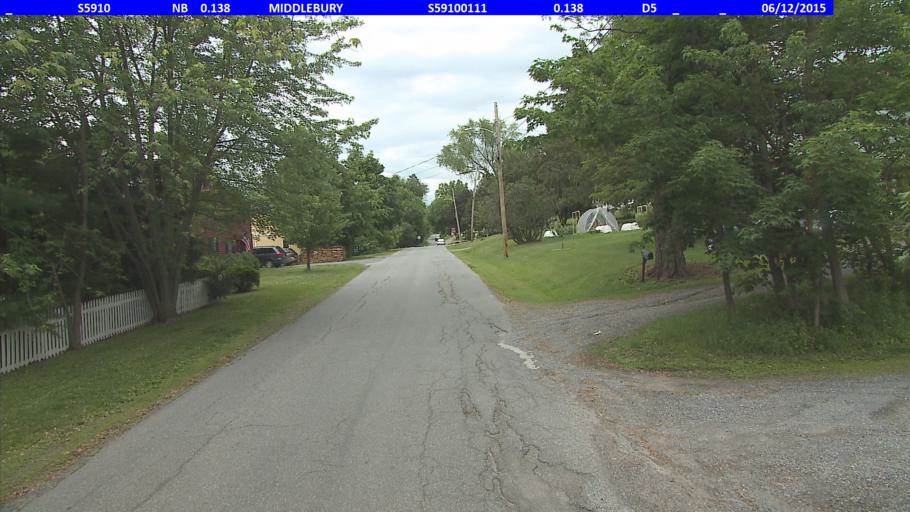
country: US
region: Vermont
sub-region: Addison County
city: Middlebury (village)
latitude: 44.0172
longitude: -73.1642
